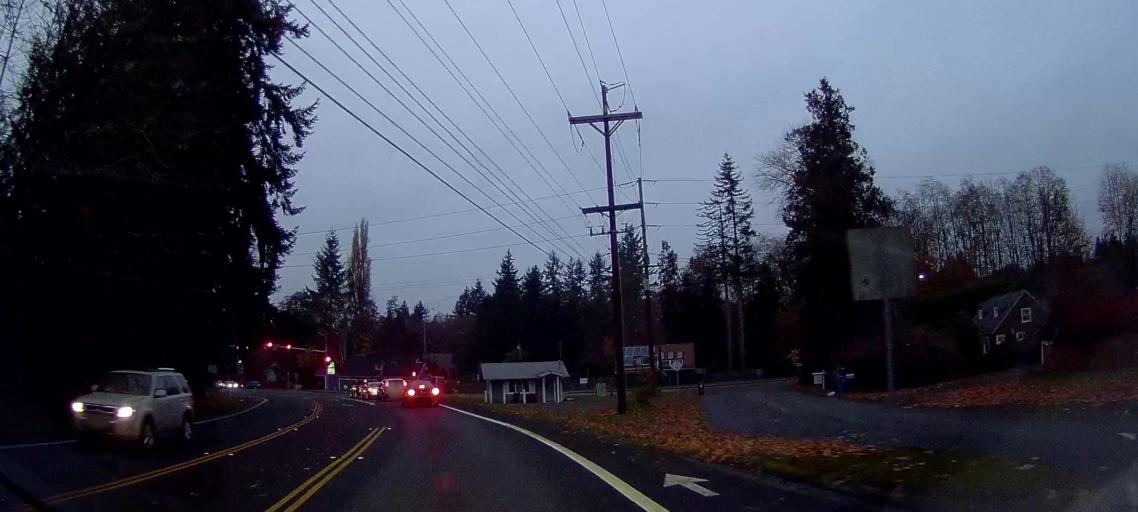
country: US
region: Washington
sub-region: Thurston County
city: Olympia
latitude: 47.0320
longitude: -122.8652
